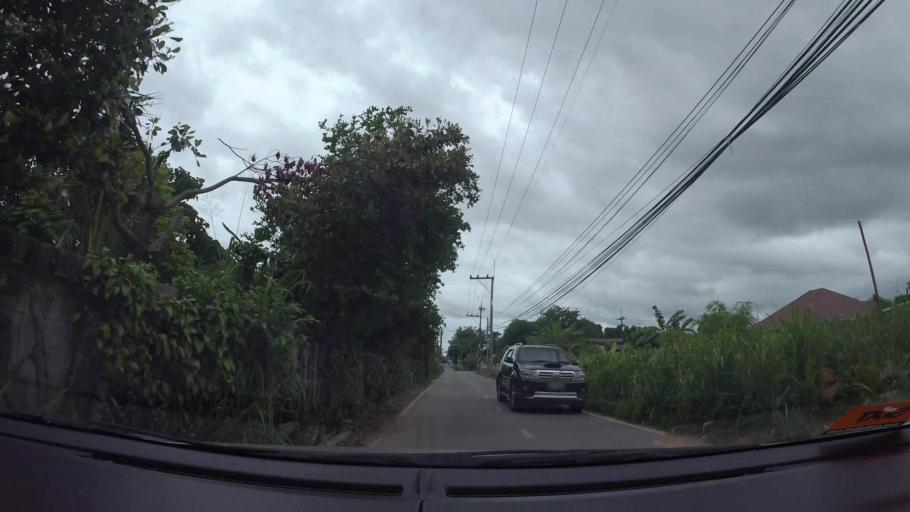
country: TH
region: Chon Buri
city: Sattahip
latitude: 12.7245
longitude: 100.9024
